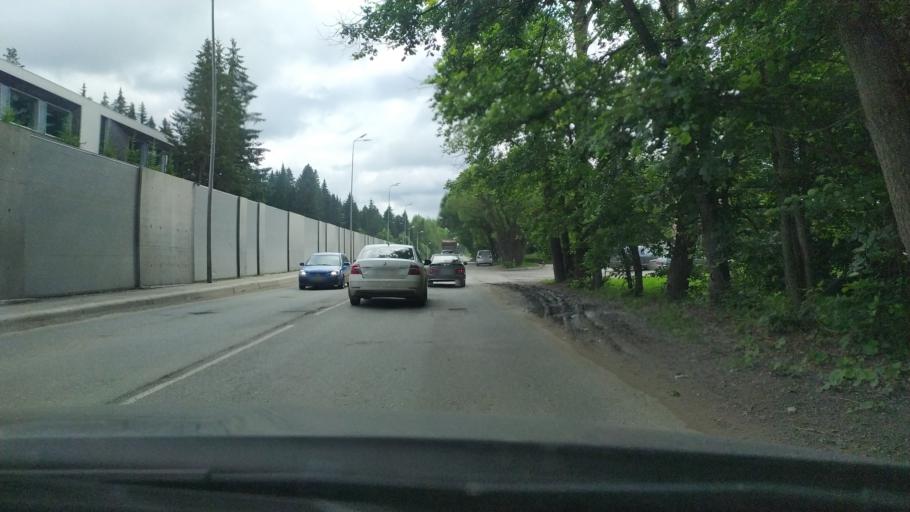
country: RU
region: Perm
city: Froly
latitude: 57.9759
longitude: 56.3184
